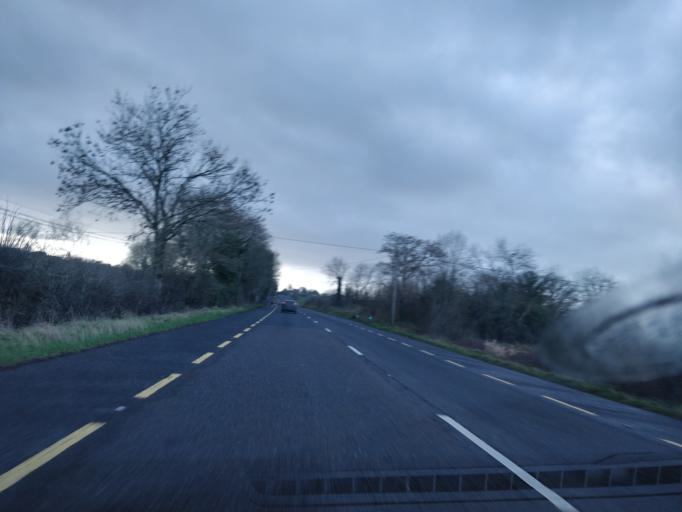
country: IE
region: Connaught
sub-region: Maigh Eo
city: Kiltamagh
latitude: 53.9035
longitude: -9.0700
